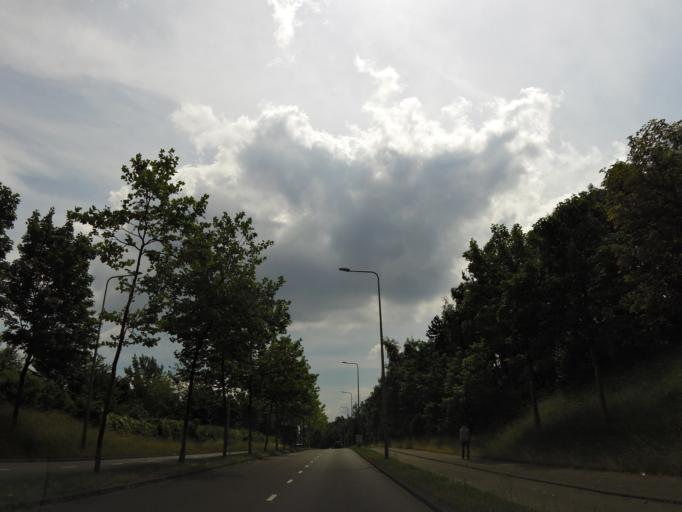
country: NL
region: Limburg
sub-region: Gemeente Heerlen
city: Heerlen
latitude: 50.8996
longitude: 5.9651
